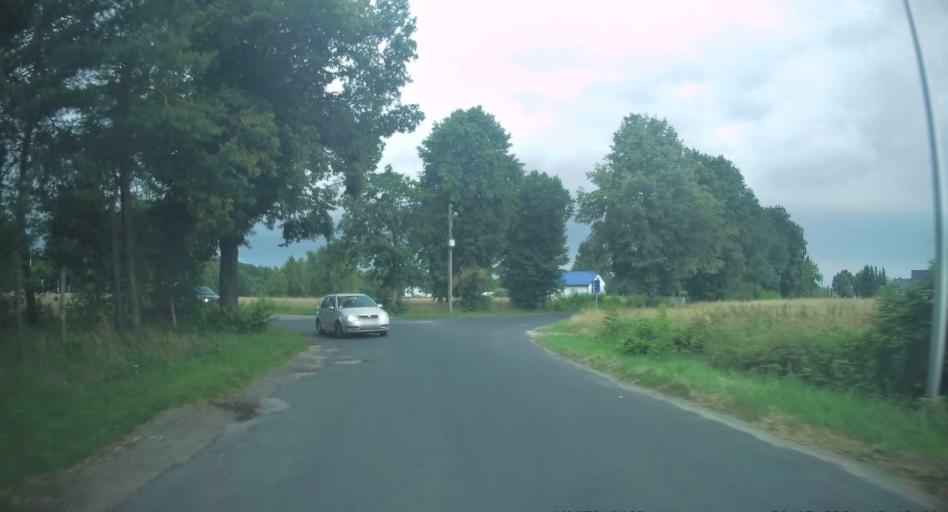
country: PL
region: Lodz Voivodeship
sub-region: Powiat rawski
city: Rawa Mazowiecka
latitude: 51.7388
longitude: 20.1928
